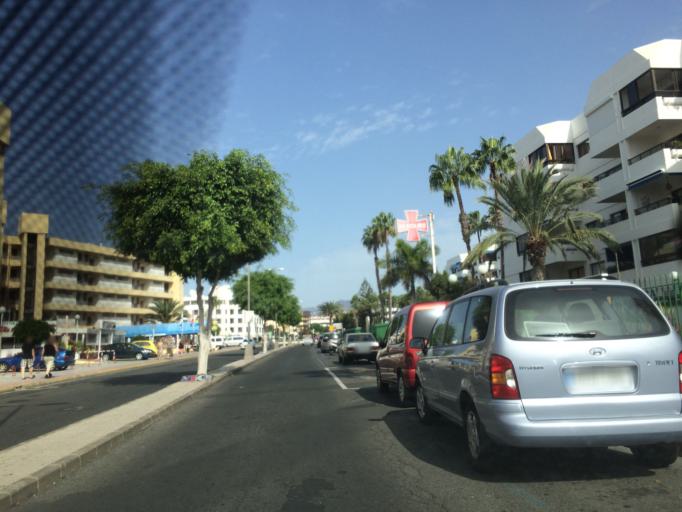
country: ES
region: Canary Islands
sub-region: Provincia de Las Palmas
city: Playa del Ingles
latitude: 27.7563
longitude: -15.5786
